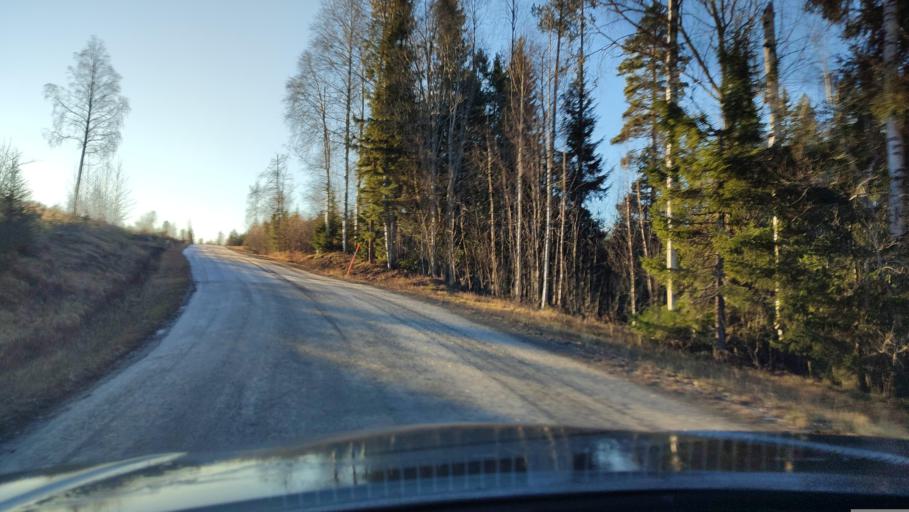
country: SE
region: Vaesterbotten
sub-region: Skelleftea Kommun
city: Viken
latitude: 64.7202
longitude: 20.9159
